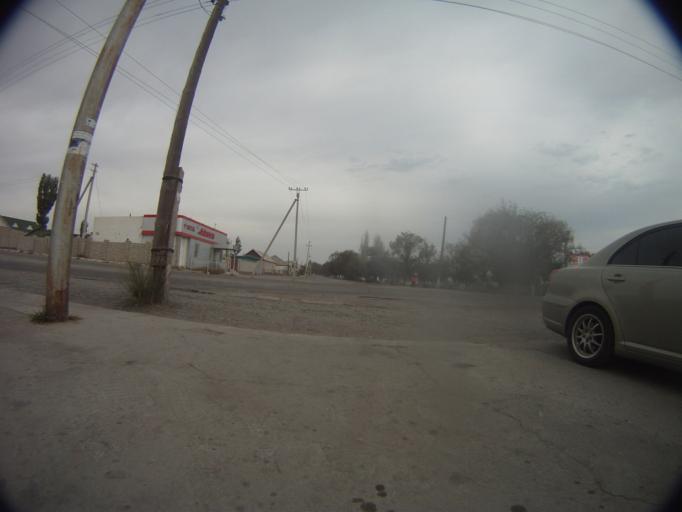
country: KG
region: Ysyk-Koel
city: Balykchy
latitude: 42.4612
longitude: 76.2101
